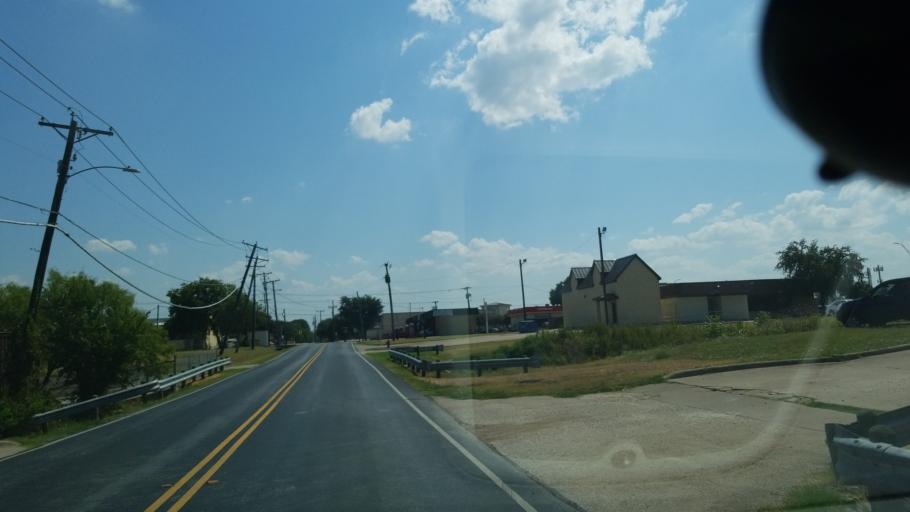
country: US
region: Texas
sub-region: Dallas County
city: Grand Prairie
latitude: 32.7103
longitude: -96.9961
